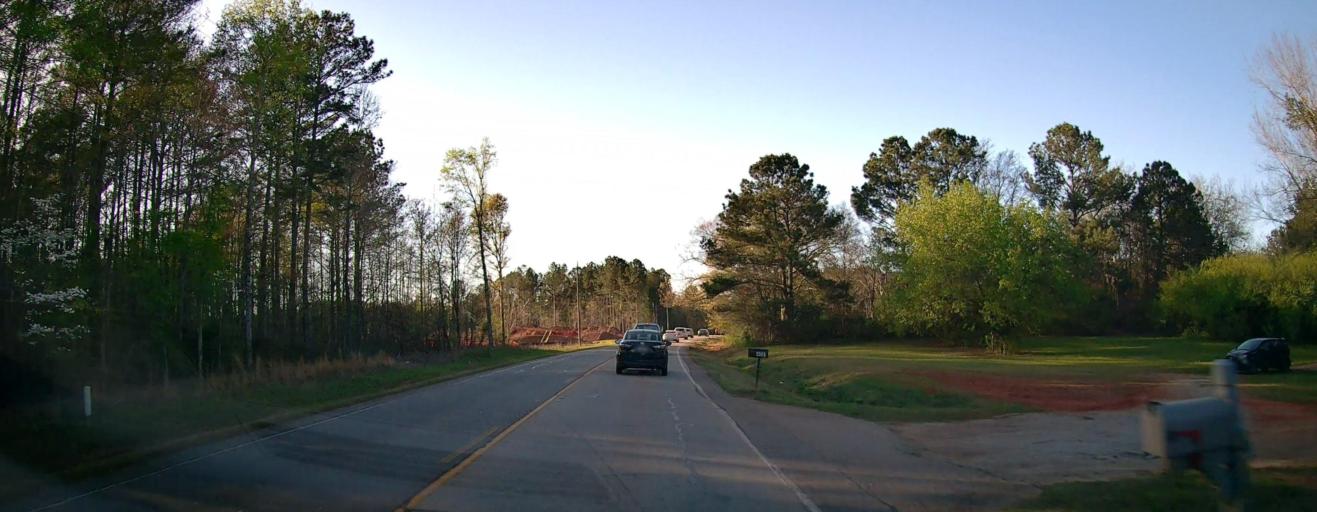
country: US
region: Georgia
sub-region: Newton County
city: Oakwood
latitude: 33.4612
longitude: -83.9065
